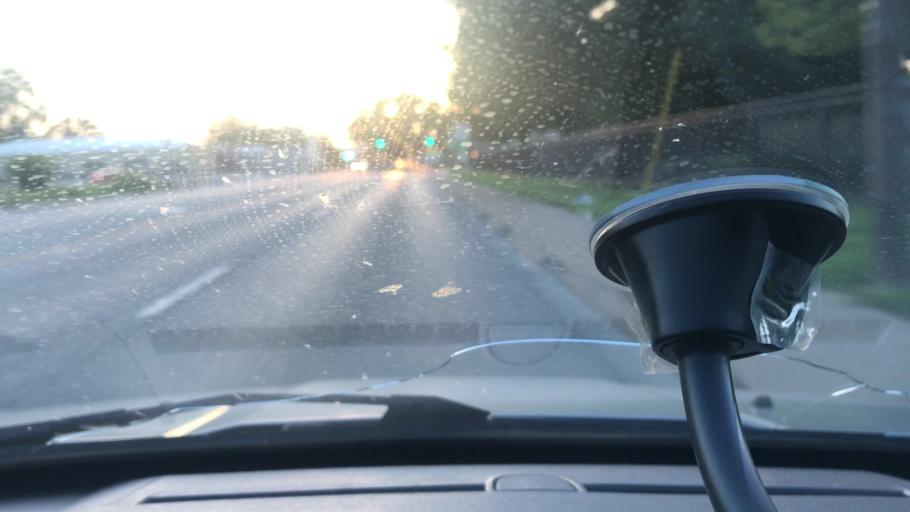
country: US
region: Illinois
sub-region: Tazewell County
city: Pekin
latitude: 40.5663
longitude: -89.6390
